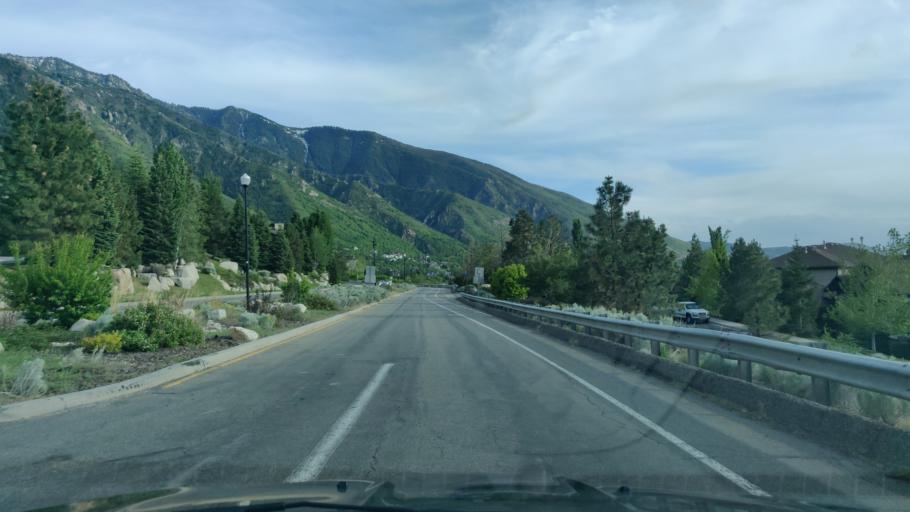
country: US
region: Utah
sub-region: Salt Lake County
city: Granite
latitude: 40.5646
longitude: -111.8040
